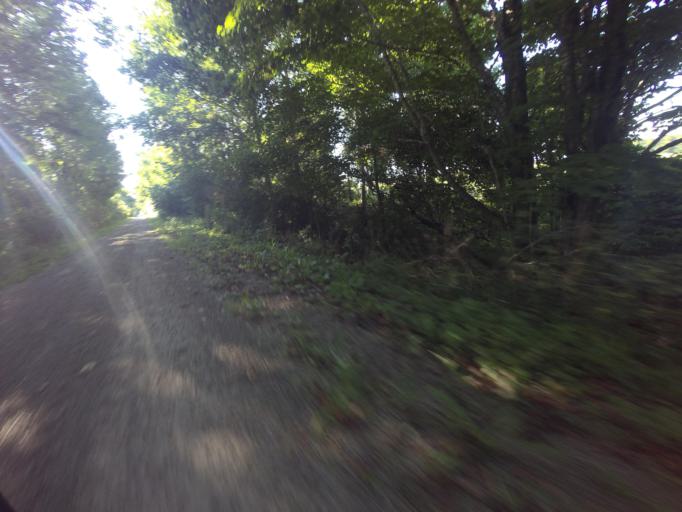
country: CA
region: Ontario
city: Goderich
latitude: 43.7495
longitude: -81.5012
